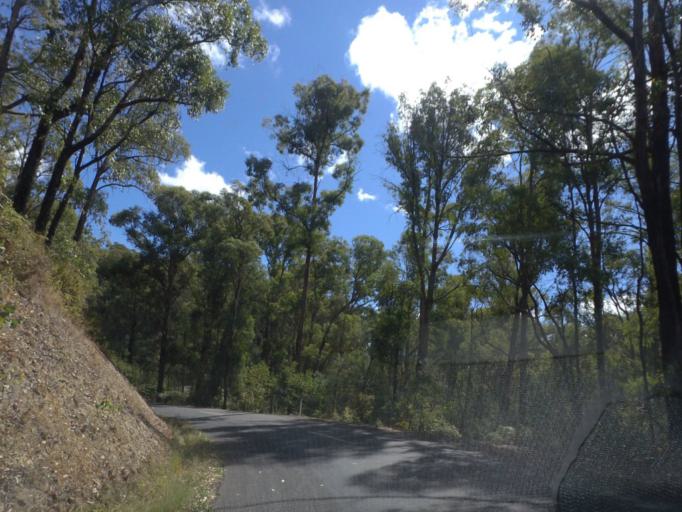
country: AU
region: Victoria
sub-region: Murrindindi
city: Alexandra
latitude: -37.3349
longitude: 145.9461
